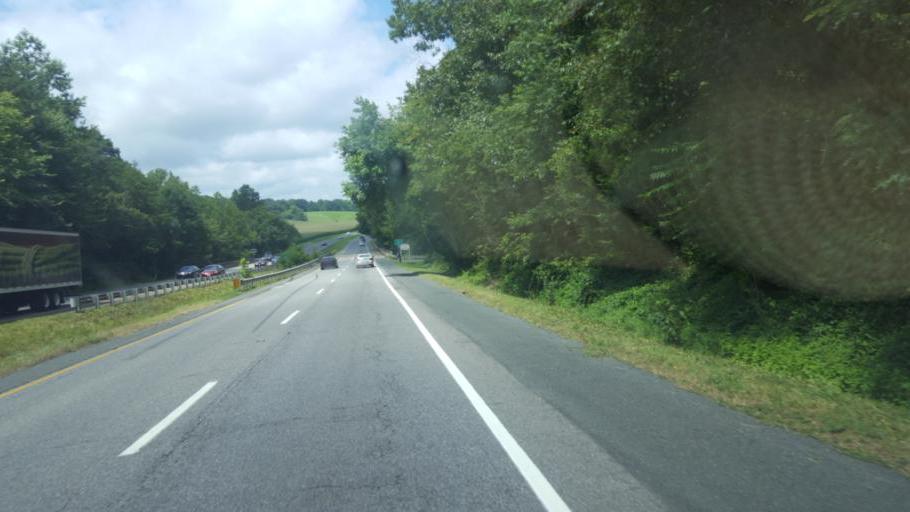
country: US
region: Virginia
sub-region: Stafford County
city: Falmouth
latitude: 38.4297
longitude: -77.6275
